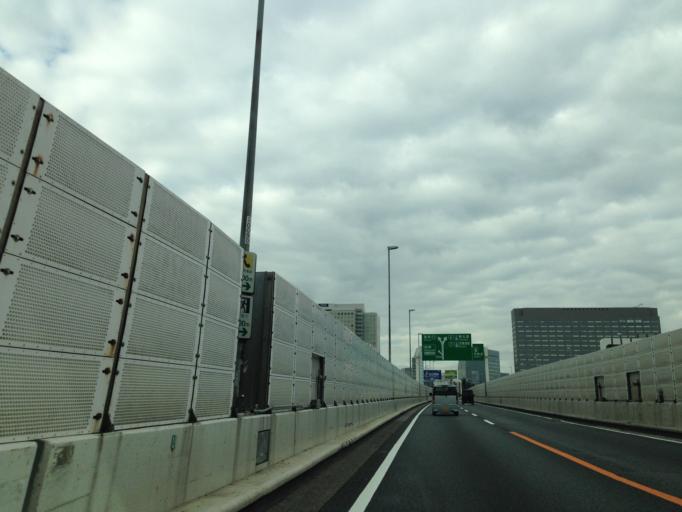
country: JP
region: Tokyo
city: Urayasu
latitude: 35.6768
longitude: 139.7939
